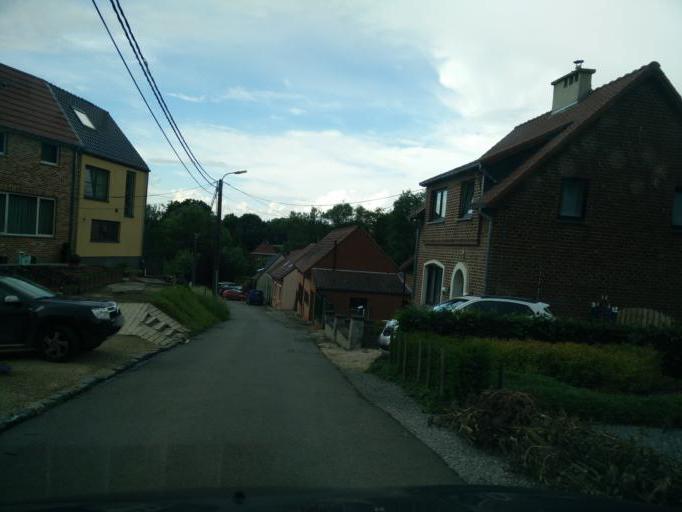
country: BE
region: Flanders
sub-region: Provincie Vlaams-Brabant
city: Beersel
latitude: 50.7184
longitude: 4.3101
